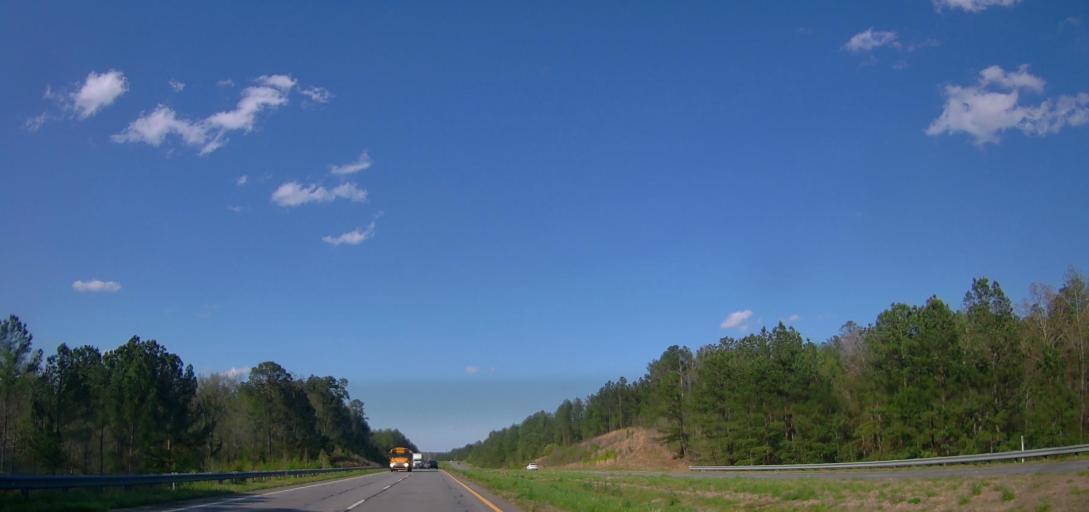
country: US
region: Georgia
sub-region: Baldwin County
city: Milledgeville
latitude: 33.0588
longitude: -83.2523
